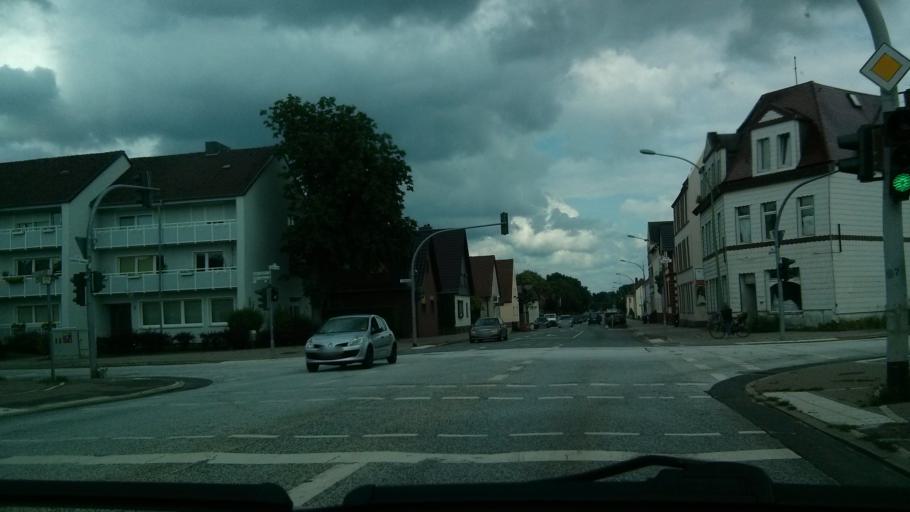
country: DE
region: Bremen
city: Bremerhaven
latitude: 53.5306
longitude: 8.6058
